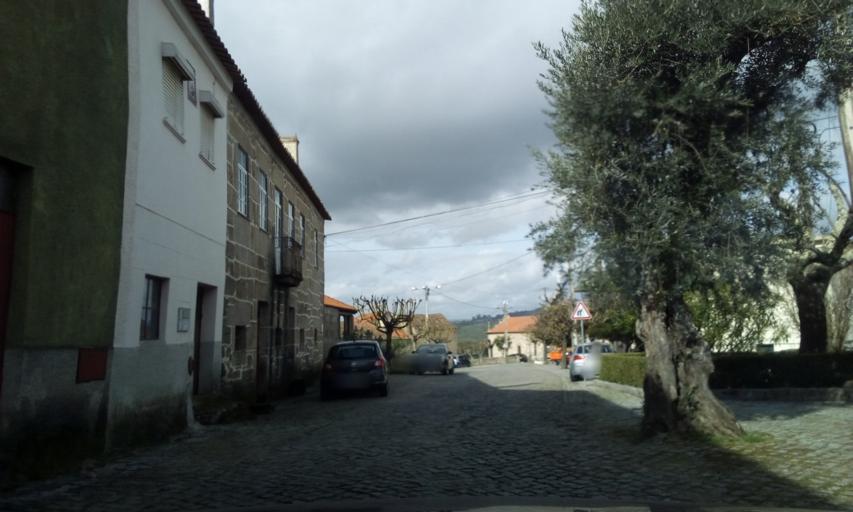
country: PT
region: Guarda
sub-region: Fornos de Algodres
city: Fornos de Algodres
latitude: 40.6617
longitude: -7.6486
